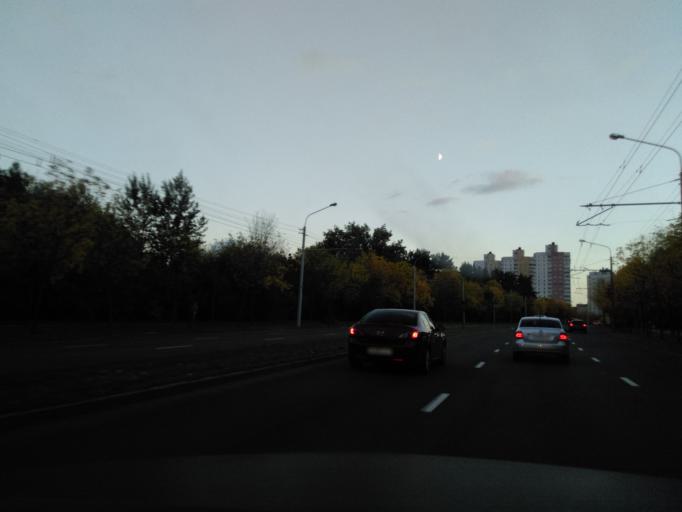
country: BY
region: Minsk
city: Minsk
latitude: 53.9150
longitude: 27.6359
